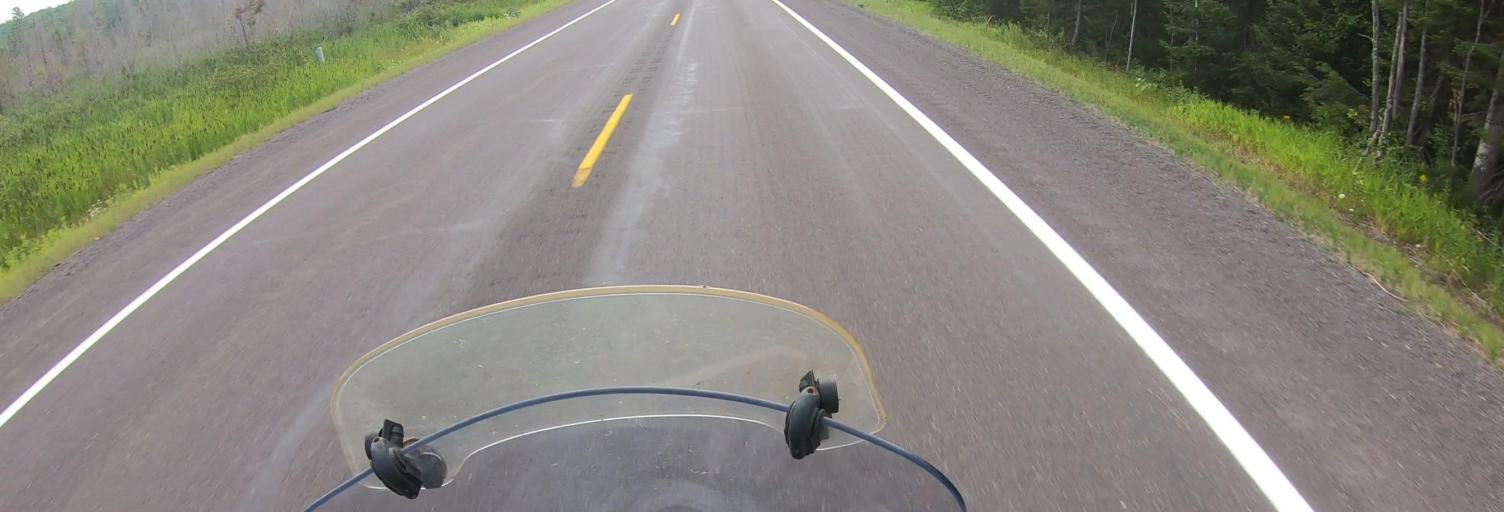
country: US
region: Michigan
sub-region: Houghton County
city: Hancock
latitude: 46.9266
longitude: -88.8080
